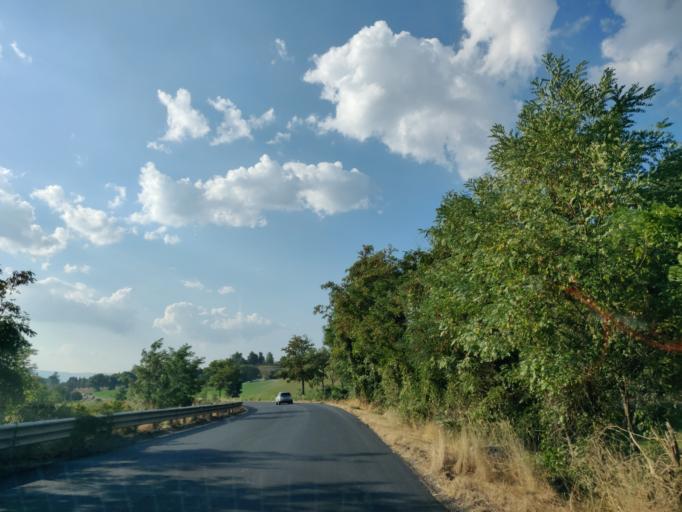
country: IT
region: Latium
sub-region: Provincia di Viterbo
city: Proceno
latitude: 42.7831
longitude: 11.8322
